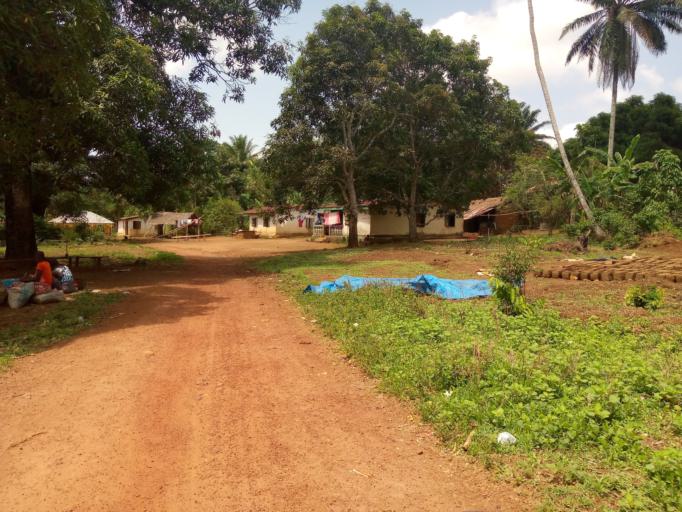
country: SL
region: Western Area
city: Waterloo
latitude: 8.3566
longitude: -12.9250
